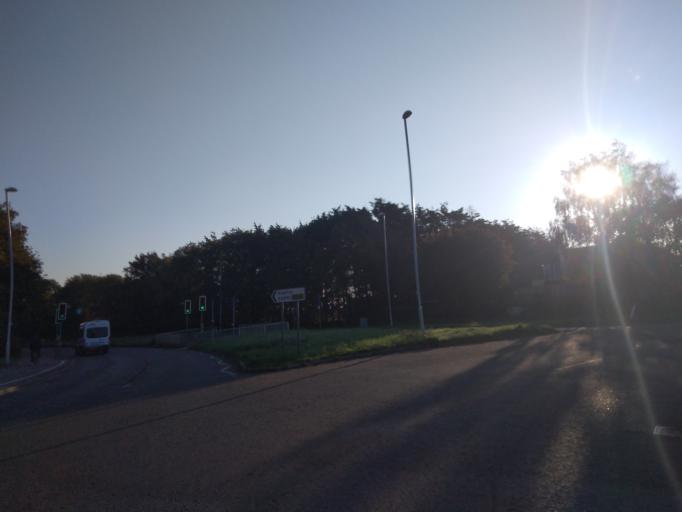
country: GB
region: England
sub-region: West Sussex
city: Goring-by-Sea
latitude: 50.8241
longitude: -0.4250
